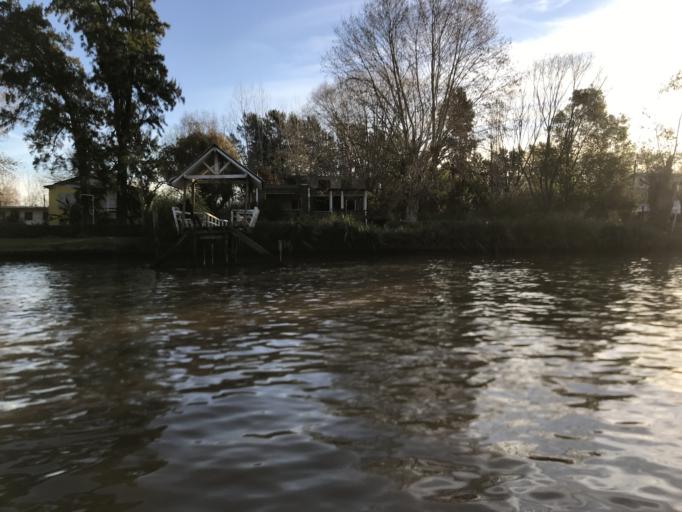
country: AR
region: Buenos Aires
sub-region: Partido de Tigre
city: Tigre
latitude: -34.3870
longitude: -58.5782
